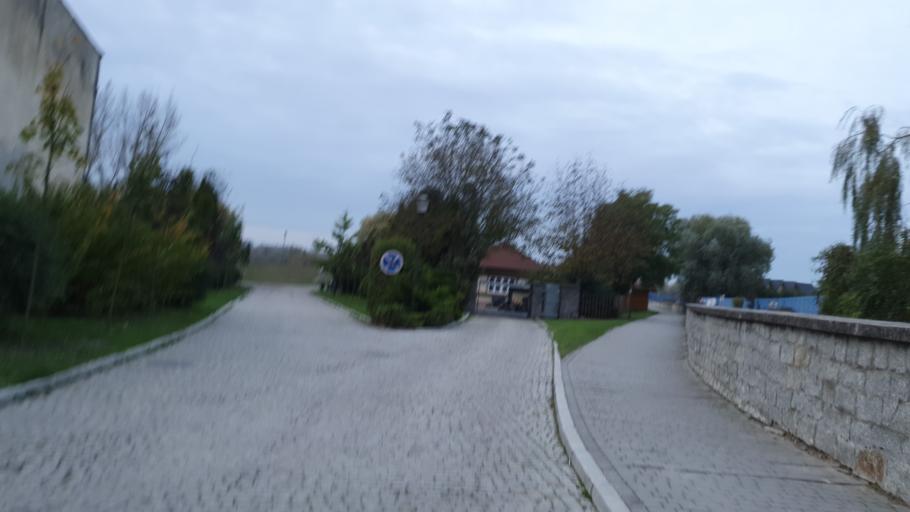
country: PL
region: Lublin Voivodeship
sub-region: Powiat pulawski
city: Kazimierz Dolny
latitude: 51.3231
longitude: 21.9447
